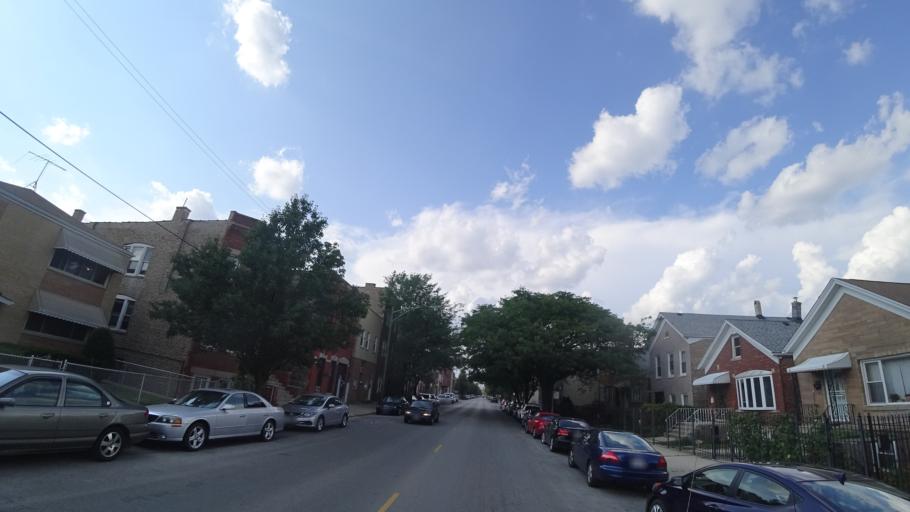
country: US
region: Illinois
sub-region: Cook County
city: Chicago
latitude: 41.8353
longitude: -87.6413
